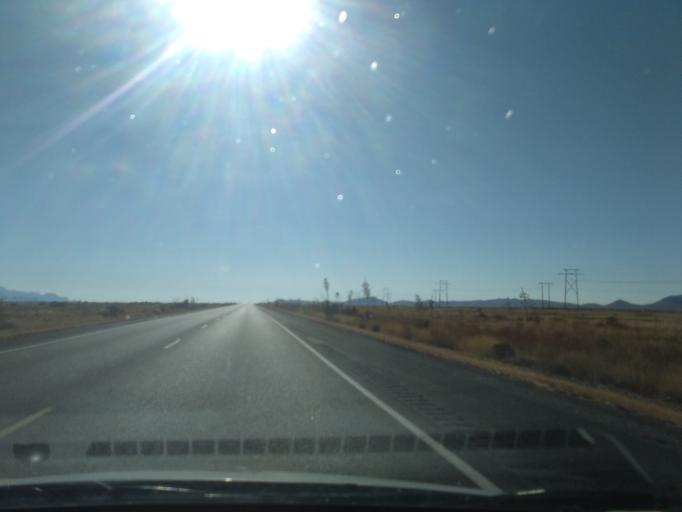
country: US
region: New Mexico
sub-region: Luna County
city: Deming
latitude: 32.4675
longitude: -107.5382
